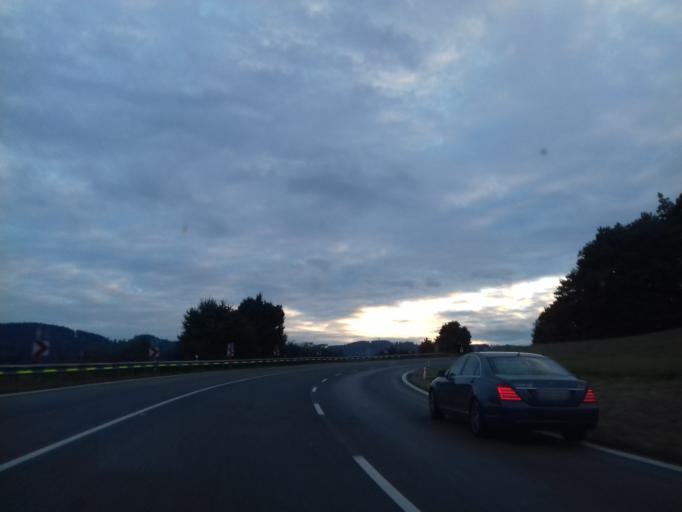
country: CZ
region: Zlin
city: Bojkovice
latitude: 48.9727
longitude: 17.8570
